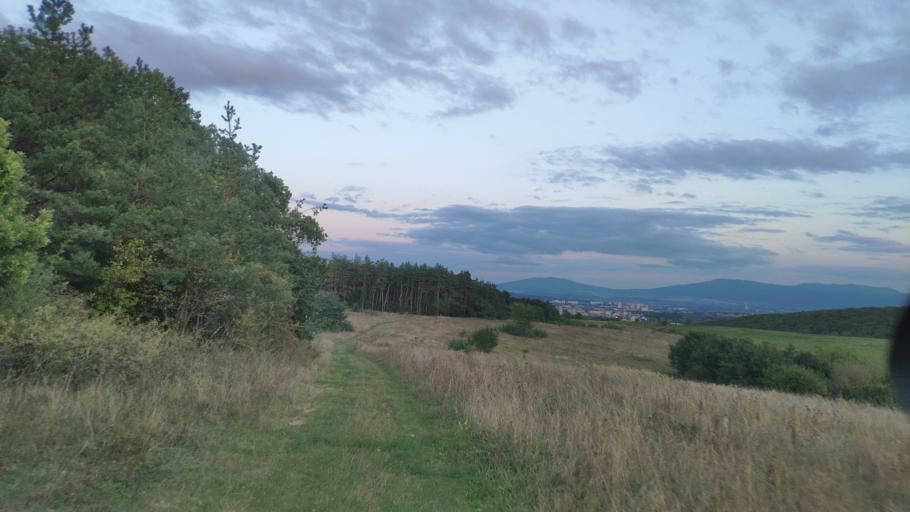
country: SK
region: Kosicky
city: Kosice
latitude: 48.7029
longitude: 21.2034
